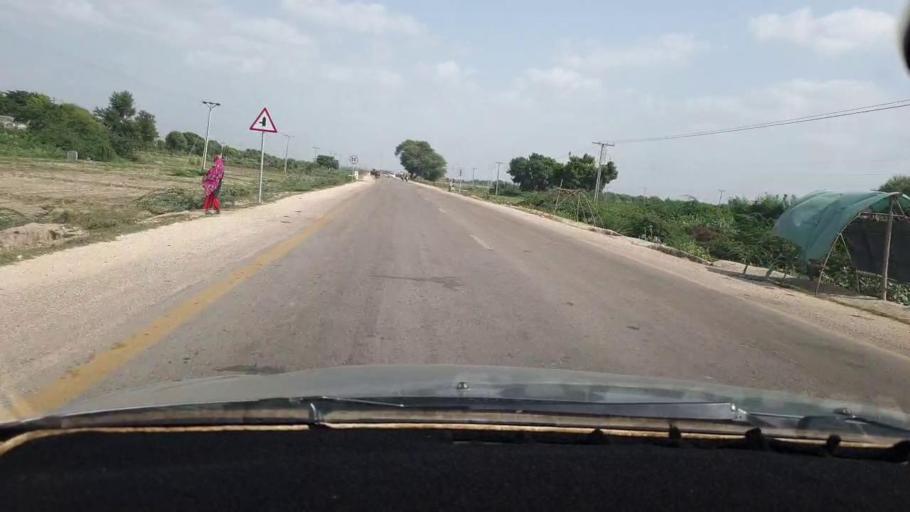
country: PK
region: Sindh
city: Naukot
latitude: 24.8756
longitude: 69.3672
